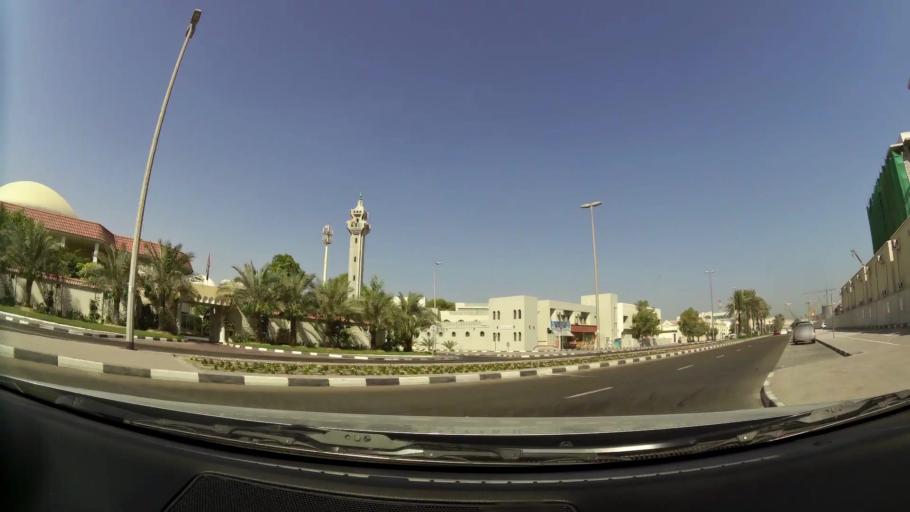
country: AE
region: Ash Shariqah
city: Sharjah
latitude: 25.2430
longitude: 55.2810
